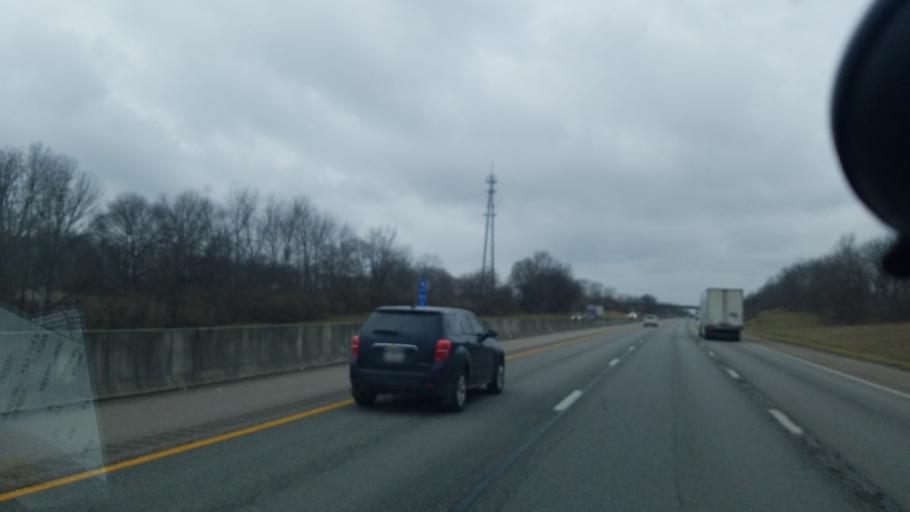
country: US
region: Kentucky
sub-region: Fayette County
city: Lexington-Fayette
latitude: 38.0509
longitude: -84.3481
